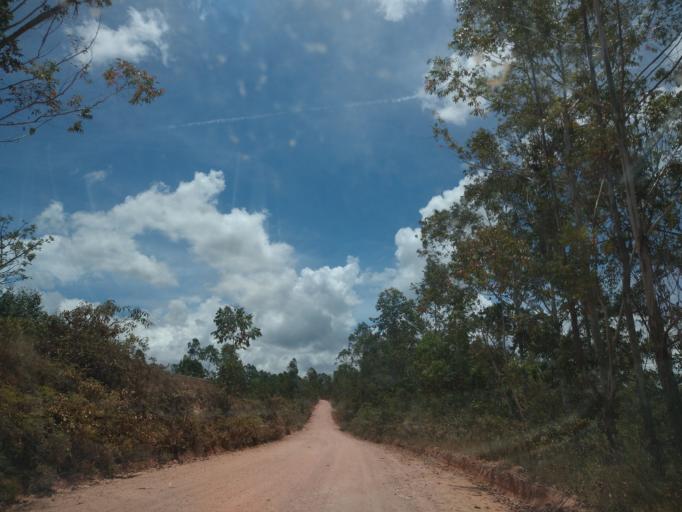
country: BR
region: Minas Gerais
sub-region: Tiradentes
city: Tiradentes
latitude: -20.9073
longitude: -44.2821
